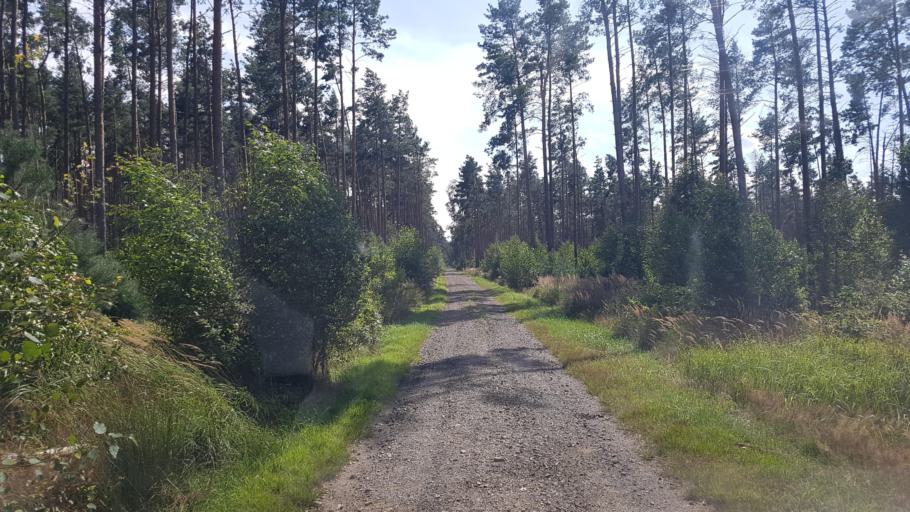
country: DE
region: Brandenburg
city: Bad Liebenwerda
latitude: 51.4928
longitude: 13.3119
